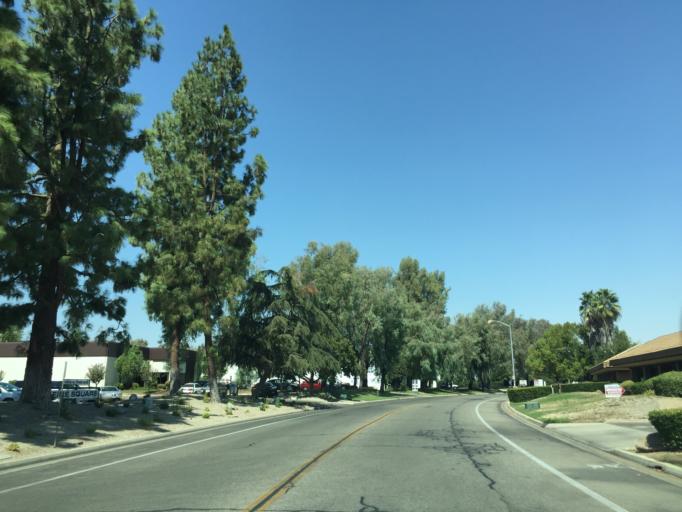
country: US
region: California
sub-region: Fresno County
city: Sunnyside
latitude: 36.7681
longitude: -119.7291
